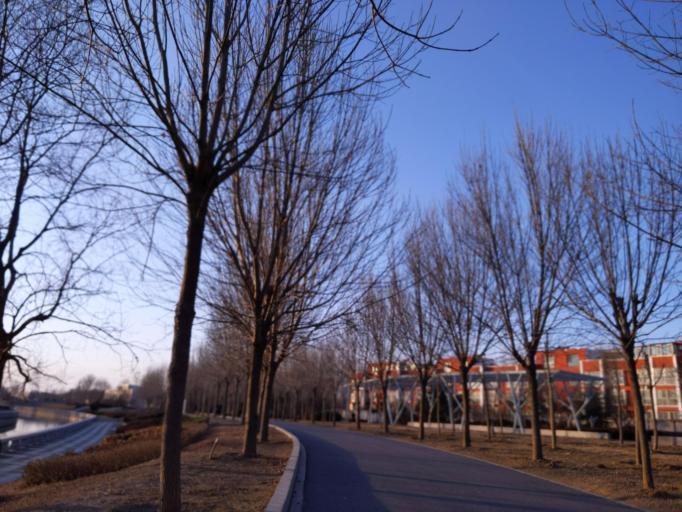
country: CN
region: Henan Sheng
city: Puyang
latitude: 35.7698
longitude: 114.9980
